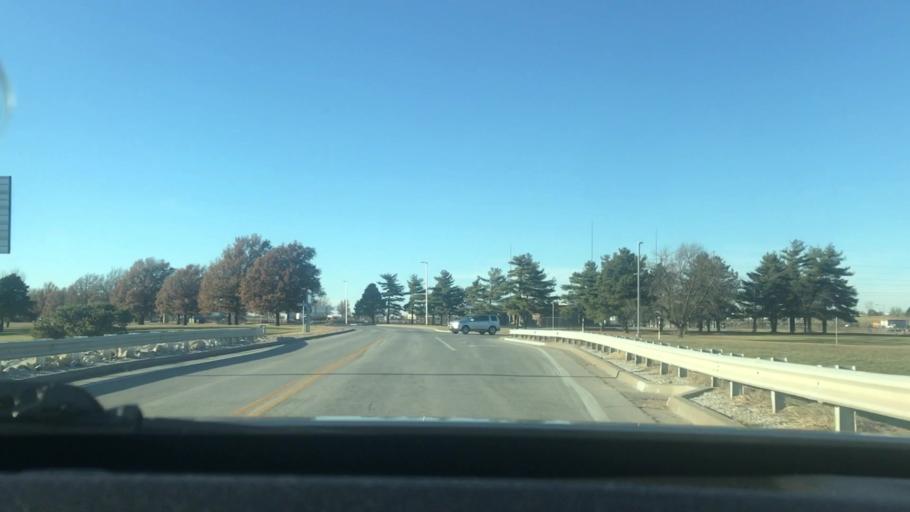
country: US
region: Missouri
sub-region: Platte County
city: Weatherby Lake
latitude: 39.3110
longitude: -94.7103
